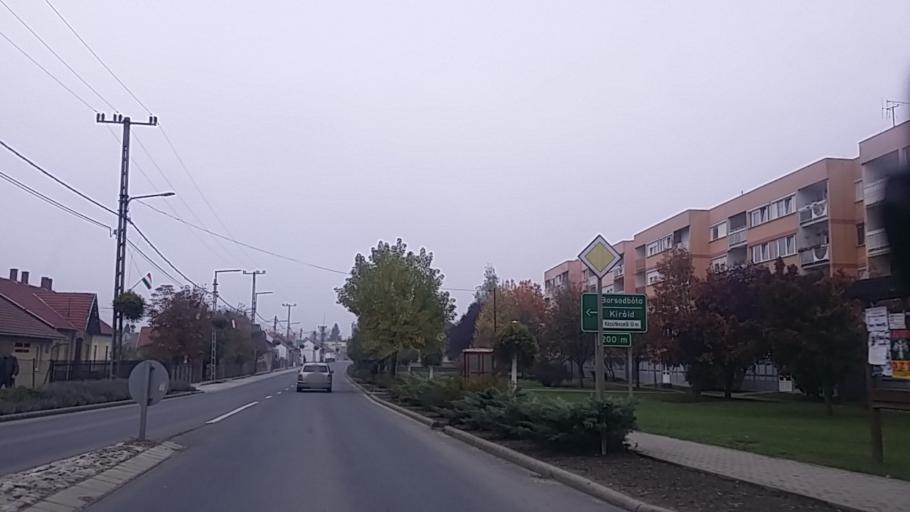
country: HU
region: Borsod-Abauj-Zemplen
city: Putnok
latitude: 48.2938
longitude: 20.4406
